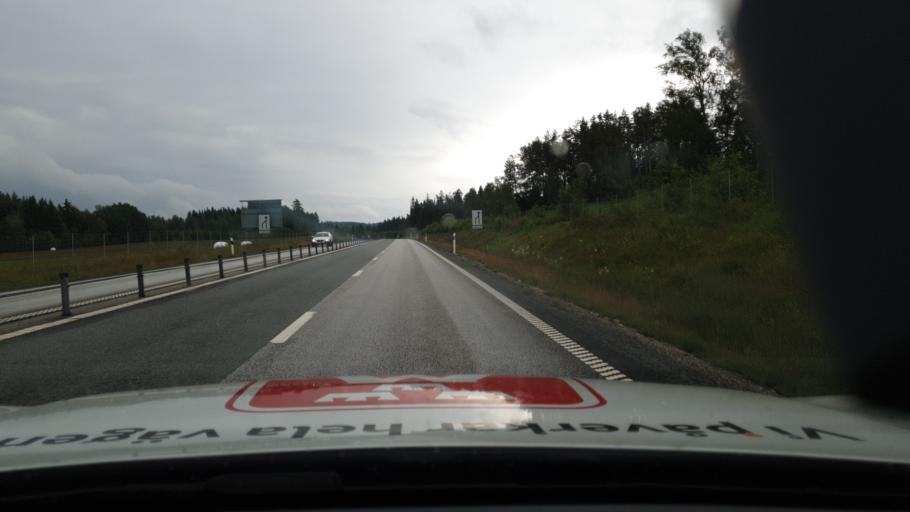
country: SE
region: Joenkoeping
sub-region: Nassjo Kommun
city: Malmback
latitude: 57.6834
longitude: 14.4698
